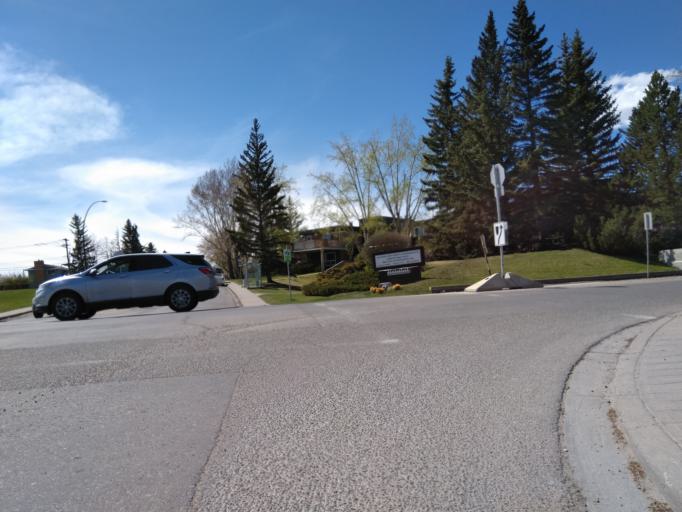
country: CA
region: Alberta
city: Calgary
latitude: 51.0126
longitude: -114.1526
